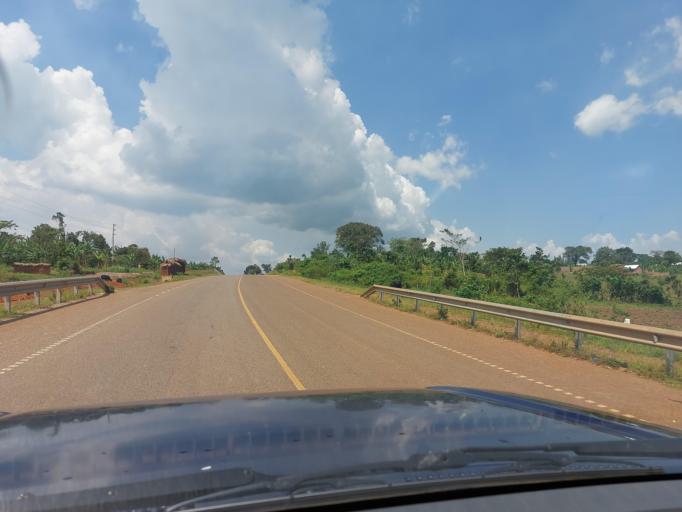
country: UG
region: Central Region
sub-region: Buikwe District
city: Buikwe
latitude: 0.3072
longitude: 33.0978
